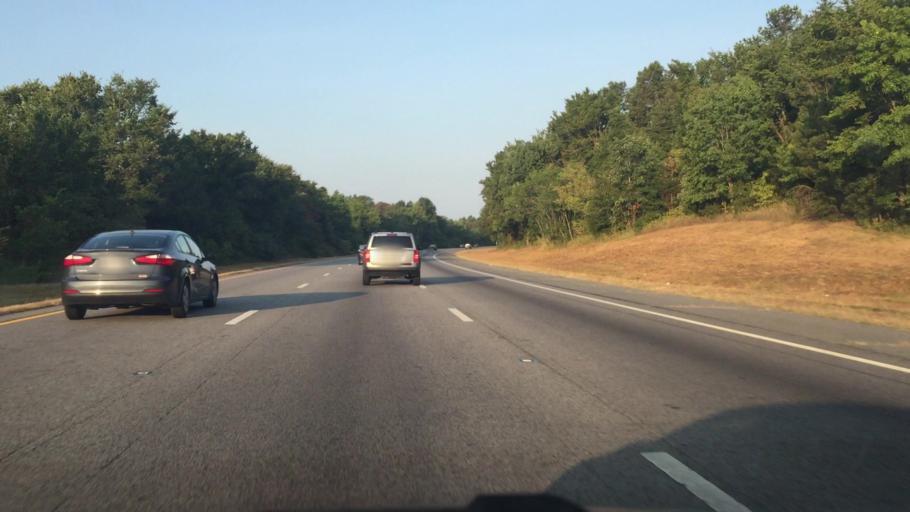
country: US
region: North Carolina
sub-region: Randolph County
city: Trinity
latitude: 35.8732
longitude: -80.0093
